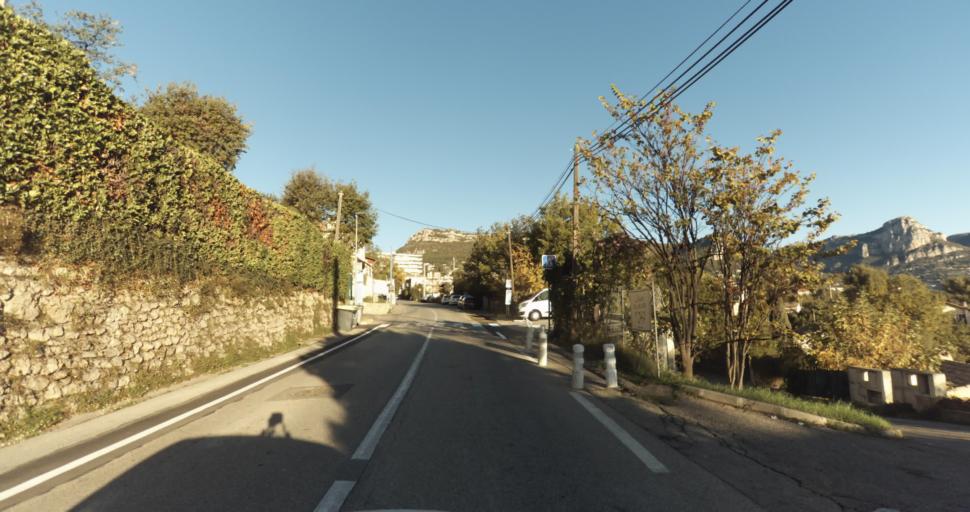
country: FR
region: Provence-Alpes-Cote d'Azur
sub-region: Departement des Alpes-Maritimes
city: Vence
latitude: 43.7187
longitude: 7.1236
